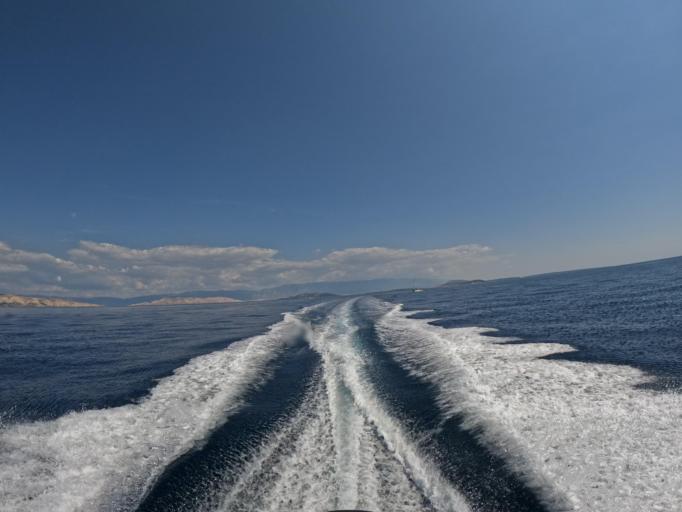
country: HR
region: Primorsko-Goranska
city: Punat
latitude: 44.9026
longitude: 14.6093
